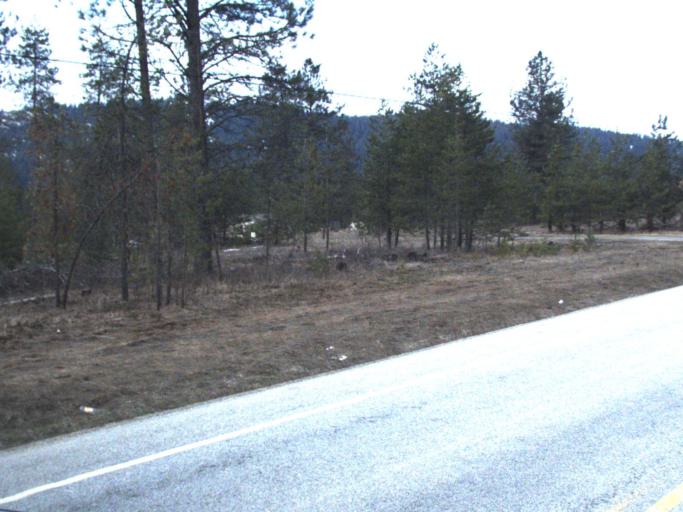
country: US
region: Washington
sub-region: Pend Oreille County
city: Newport
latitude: 48.2230
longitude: -117.1176
